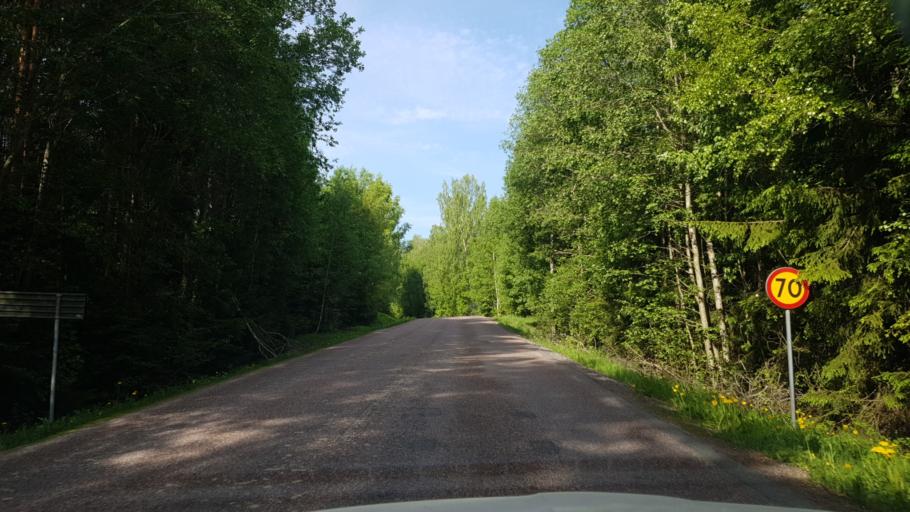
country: SE
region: Dalarna
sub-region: Saters Kommun
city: Saeter
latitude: 60.4151
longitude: 15.6970
